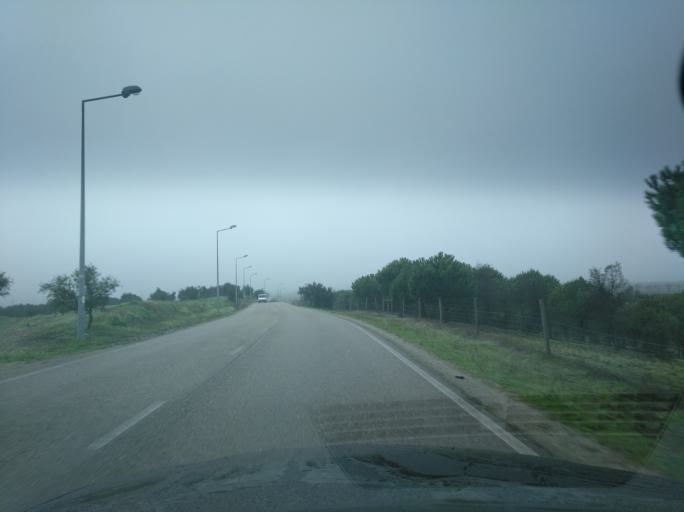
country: PT
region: Portalegre
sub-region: Campo Maior
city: Campo Maior
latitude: 39.0237
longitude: -7.0749
